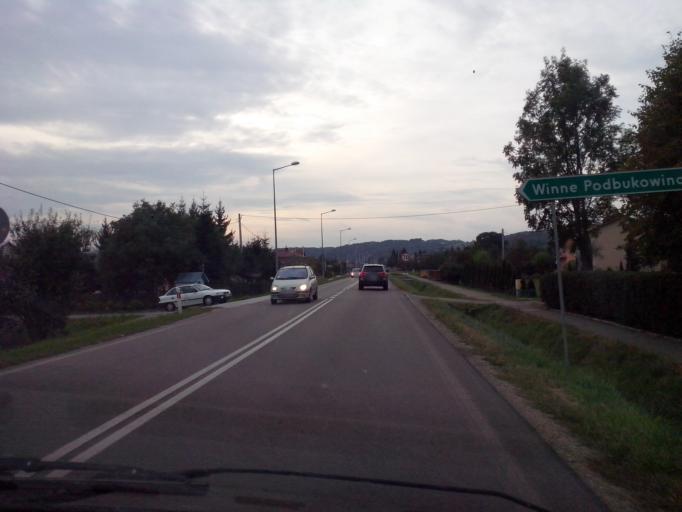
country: PL
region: Subcarpathian Voivodeship
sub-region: Powiat przemyski
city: Dubiecko
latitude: 49.8273
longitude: 22.3832
